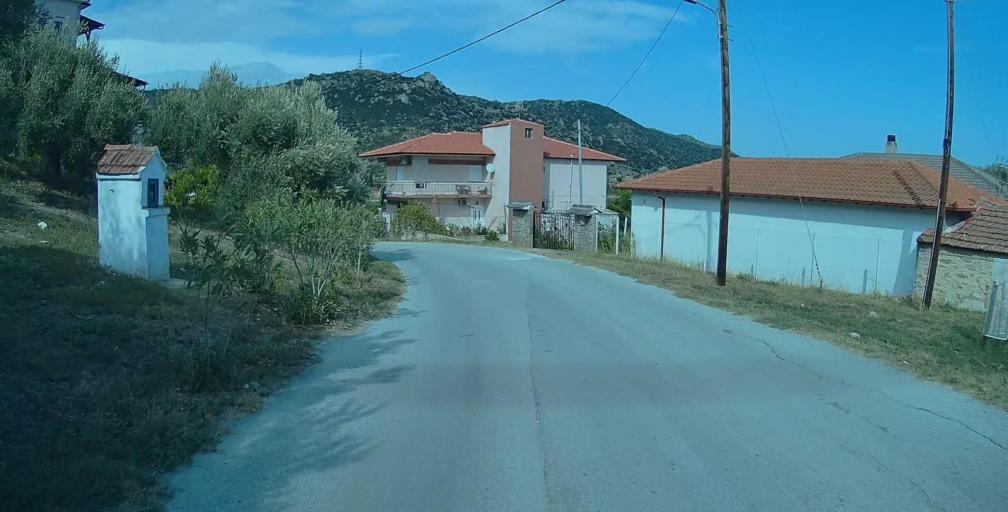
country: GR
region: Central Macedonia
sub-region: Nomos Chalkidikis
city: Sykia
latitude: 40.0372
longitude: 23.9435
